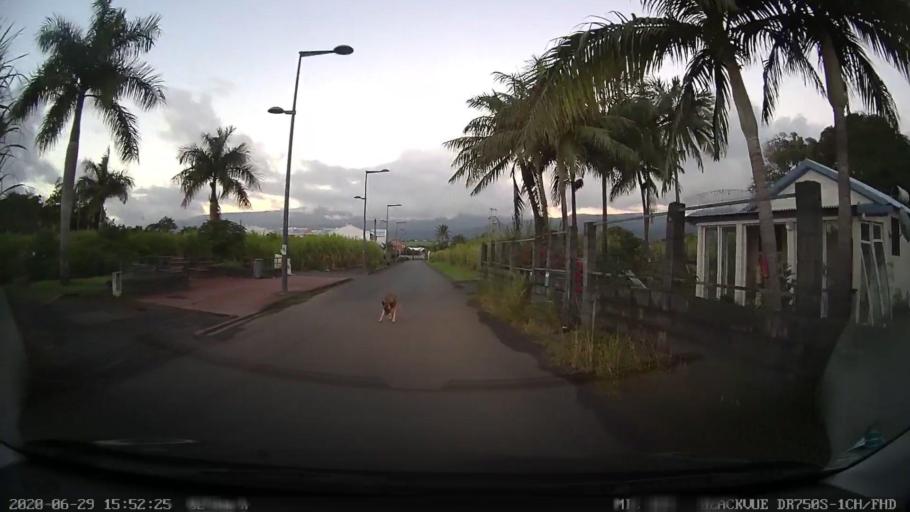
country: RE
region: Reunion
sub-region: Reunion
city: Bras-Panon
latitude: -20.9976
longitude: 55.6941
